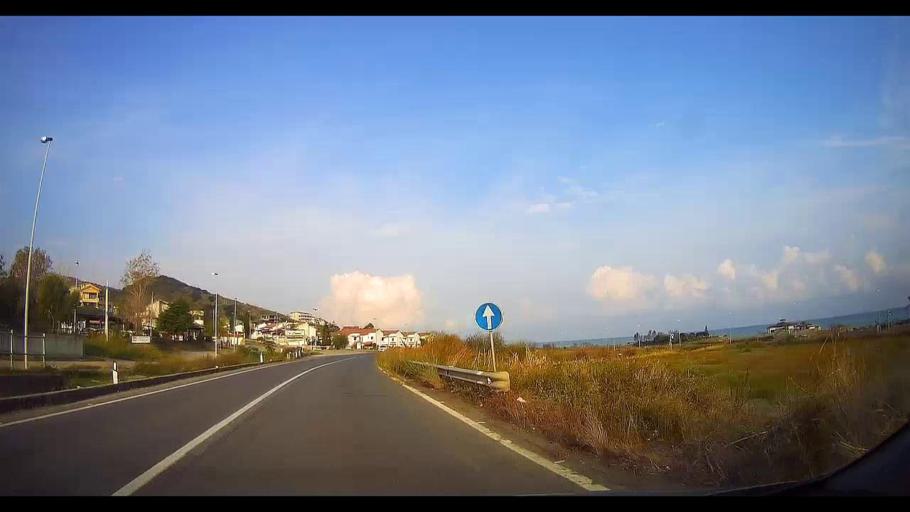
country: IT
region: Calabria
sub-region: Provincia di Cosenza
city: Cariati
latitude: 39.5258
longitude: 16.8901
